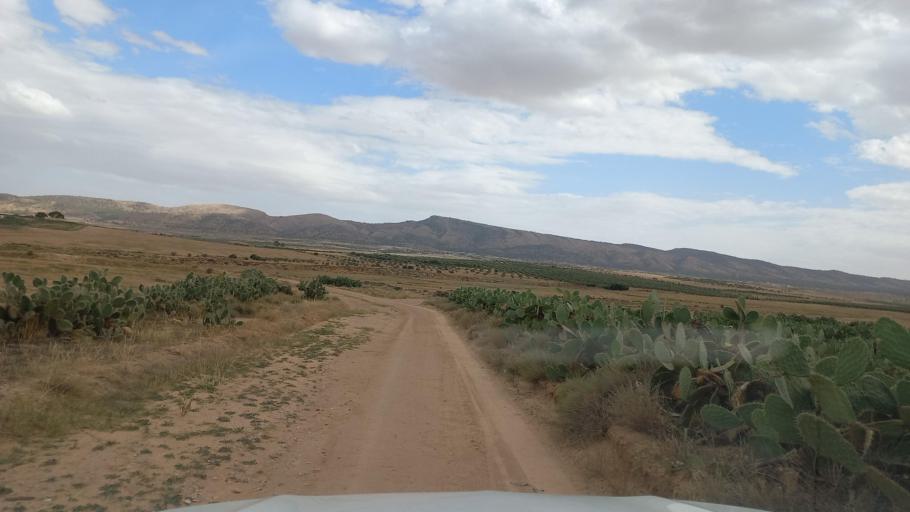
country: TN
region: Al Qasrayn
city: Sbiba
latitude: 35.3784
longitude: 9.1204
